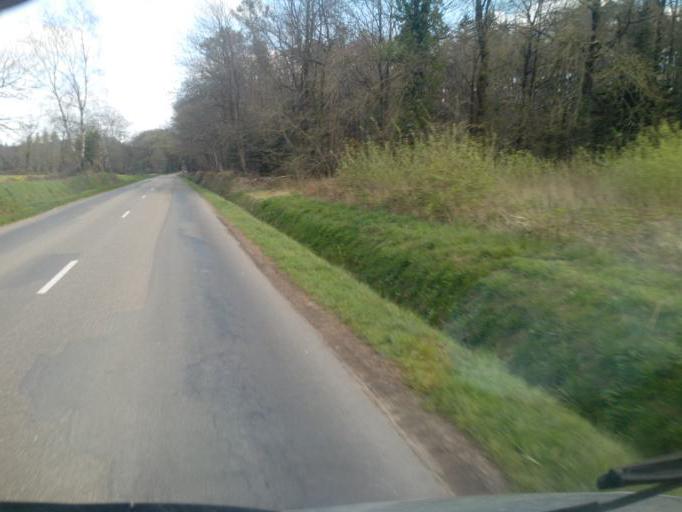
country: FR
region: Brittany
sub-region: Departement d'Ille-et-Vilaine
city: Maxent
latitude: 47.9877
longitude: -2.0551
